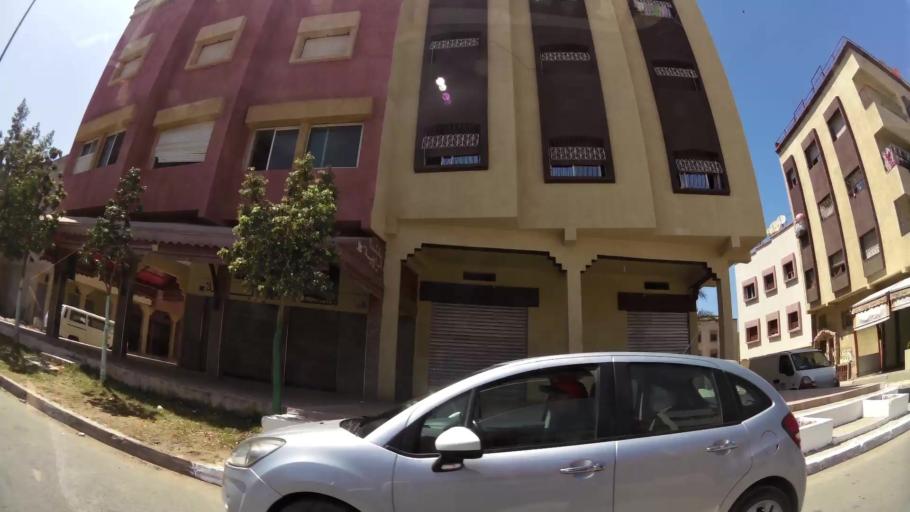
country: MA
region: Gharb-Chrarda-Beni Hssen
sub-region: Kenitra Province
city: Kenitra
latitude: 34.2465
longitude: -6.5381
